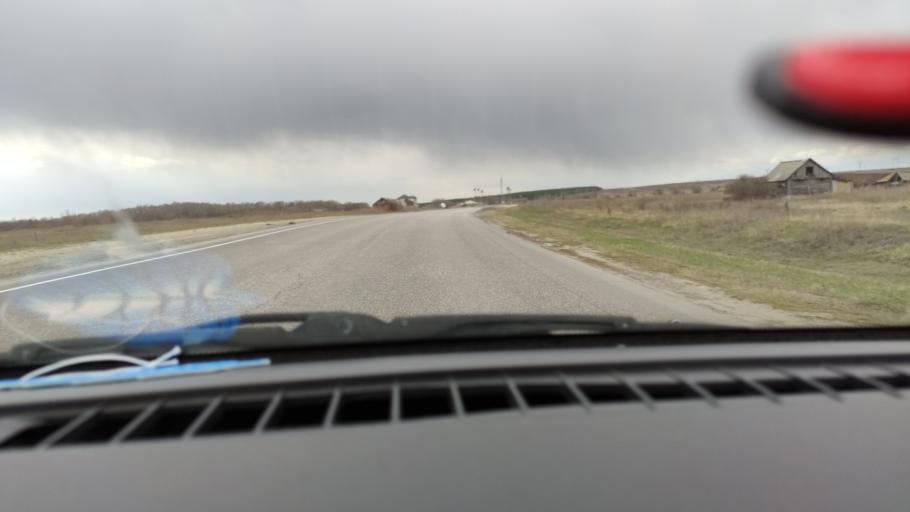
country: RU
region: Saratov
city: Sinodskoye
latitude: 52.0493
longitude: 46.7476
